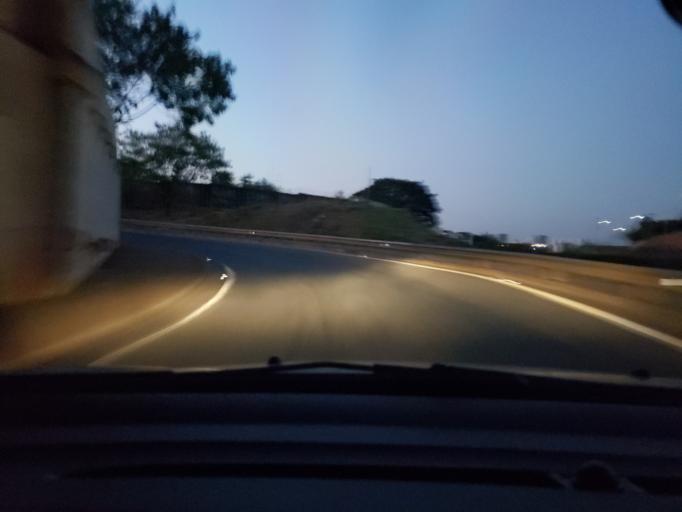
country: BR
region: Sao Paulo
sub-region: Campinas
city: Campinas
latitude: -22.9183
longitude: -47.0949
